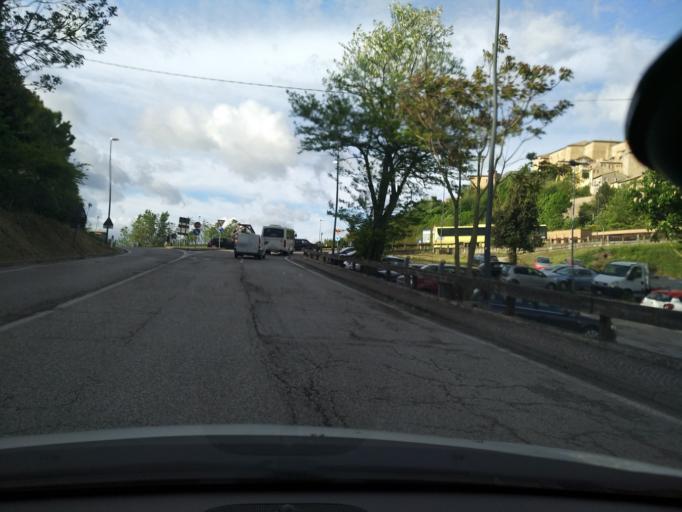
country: IT
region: The Marches
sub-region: Provincia di Pesaro e Urbino
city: Urbino
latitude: 43.7265
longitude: 12.6413
